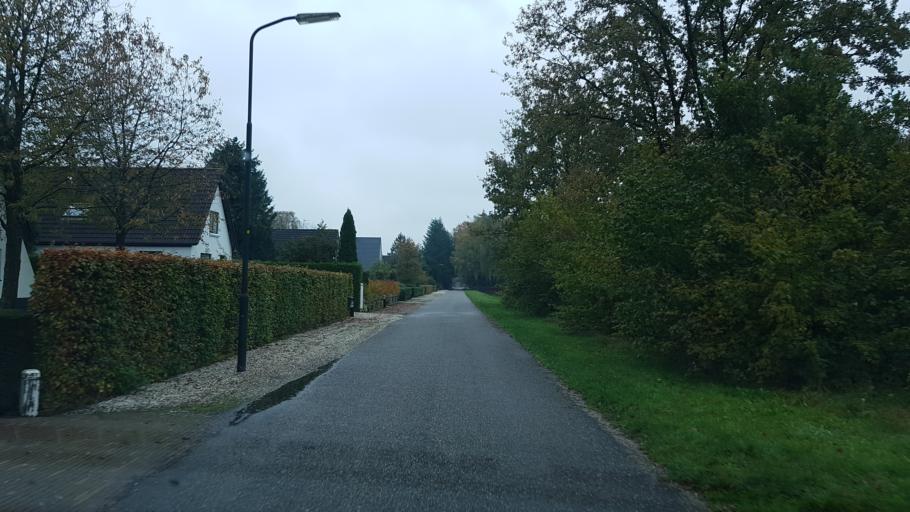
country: NL
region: Gelderland
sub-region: Gemeente Epe
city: Vaassen
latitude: 52.2492
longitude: 5.9482
